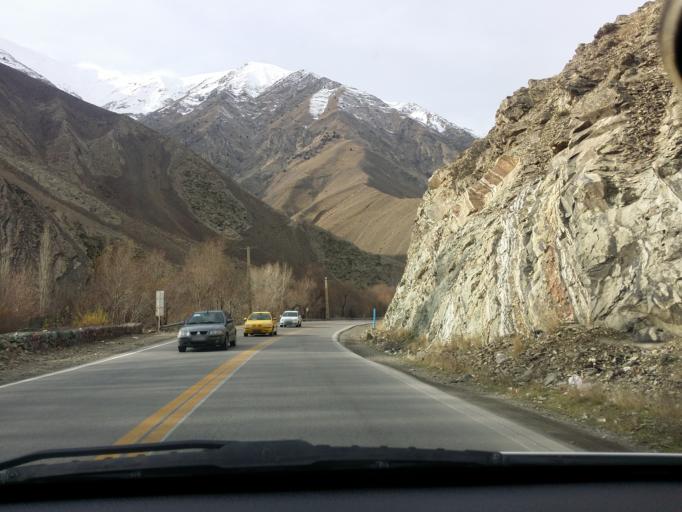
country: IR
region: Alborz
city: Karaj
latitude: 36.0320
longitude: 51.2204
